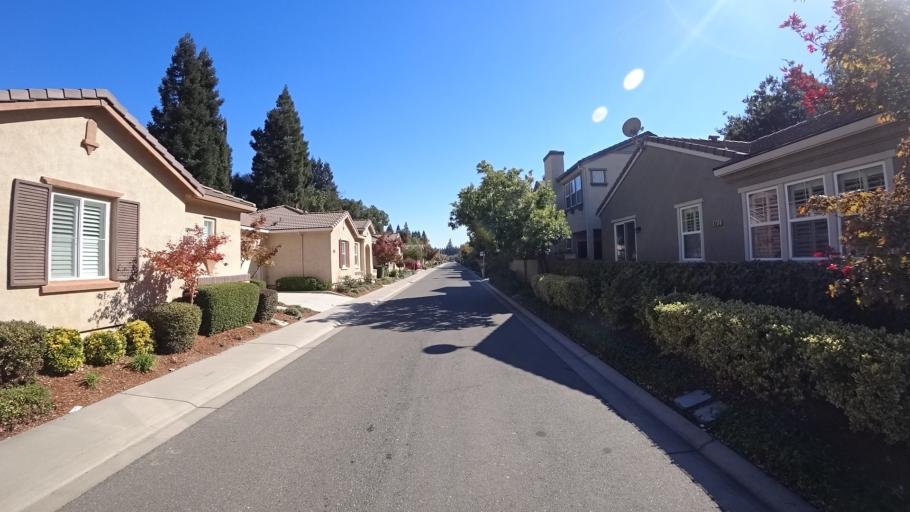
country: US
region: California
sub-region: Sacramento County
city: Parkway
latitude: 38.4771
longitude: -121.5305
